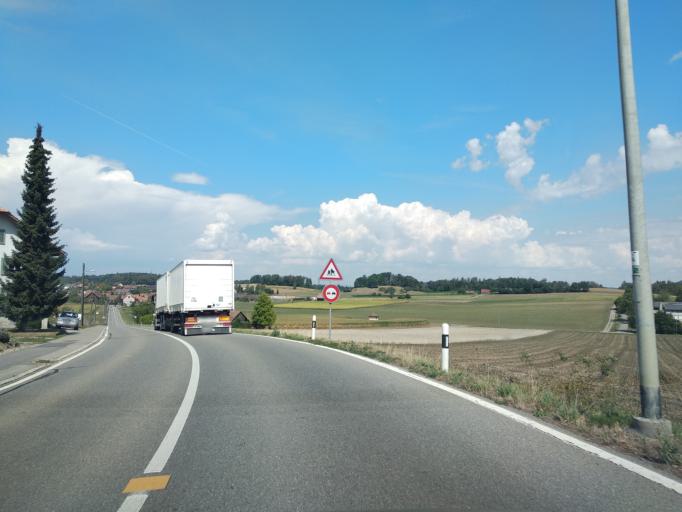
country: CH
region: Zurich
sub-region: Bezirk Winterthur
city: Sulz
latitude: 47.6004
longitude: 8.7763
